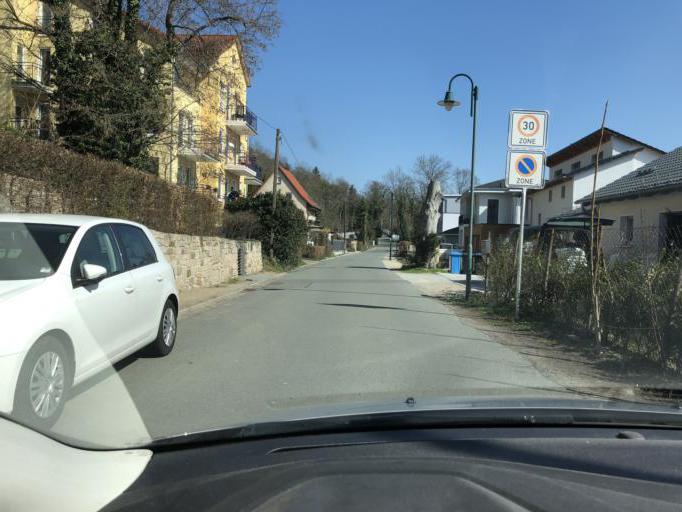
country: DE
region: Thuringia
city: Rudolstadt
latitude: 50.7213
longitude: 11.3279
